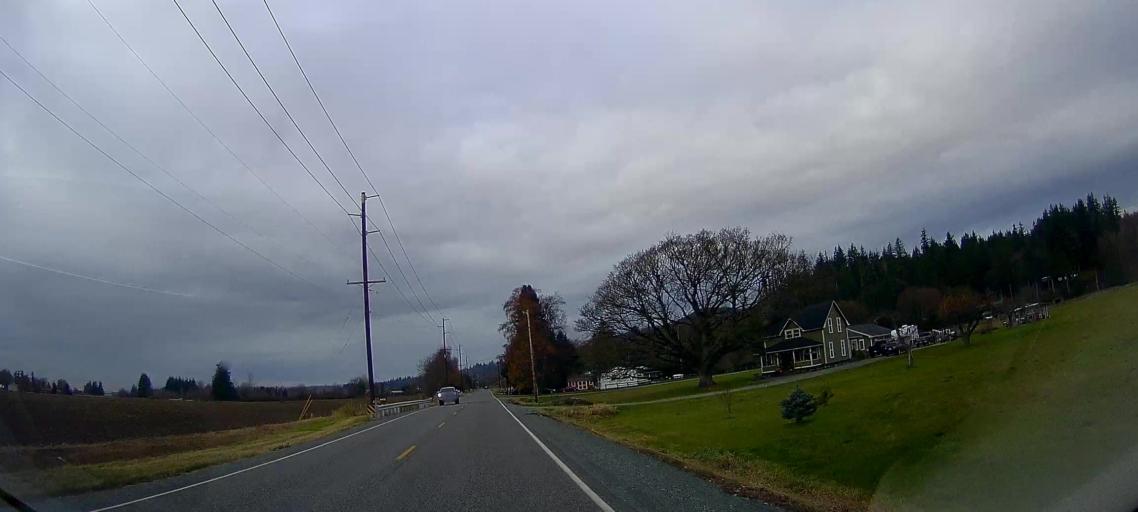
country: US
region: Washington
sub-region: Skagit County
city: Sedro-Woolley
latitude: 48.5176
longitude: -122.2604
